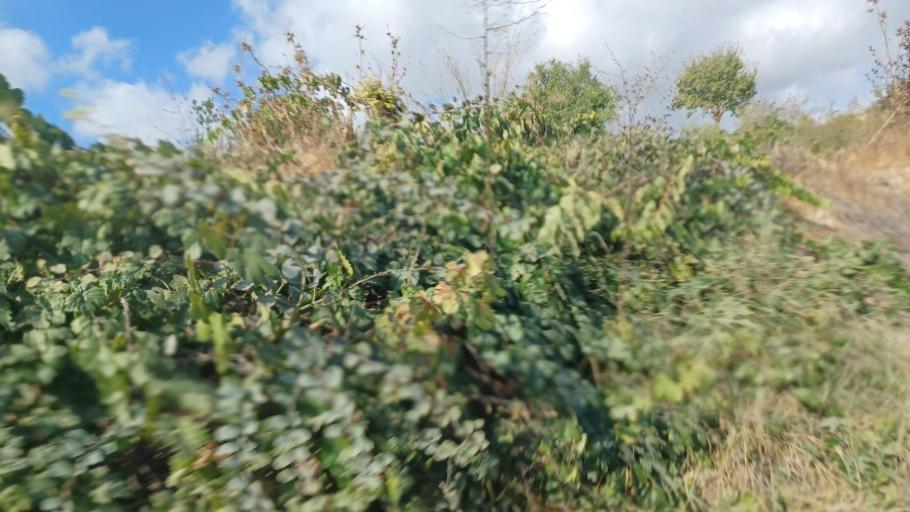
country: CY
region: Pafos
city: Mesogi
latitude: 34.8495
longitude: 32.5372
